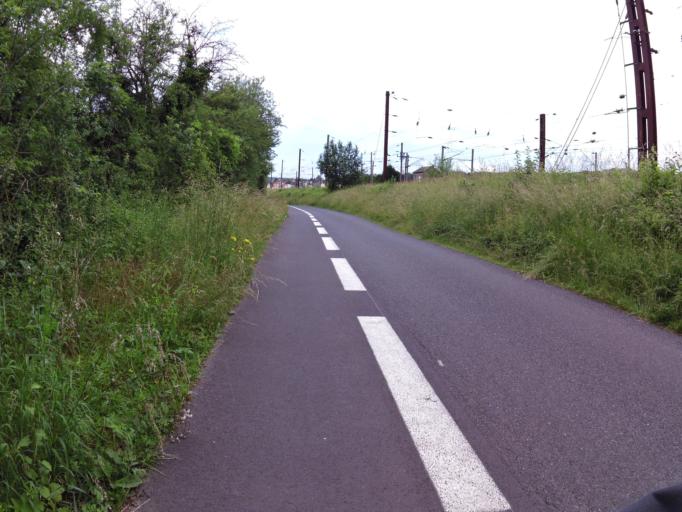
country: FR
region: Champagne-Ardenne
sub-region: Departement des Ardennes
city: Lumes
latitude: 49.7258
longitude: 4.7844
